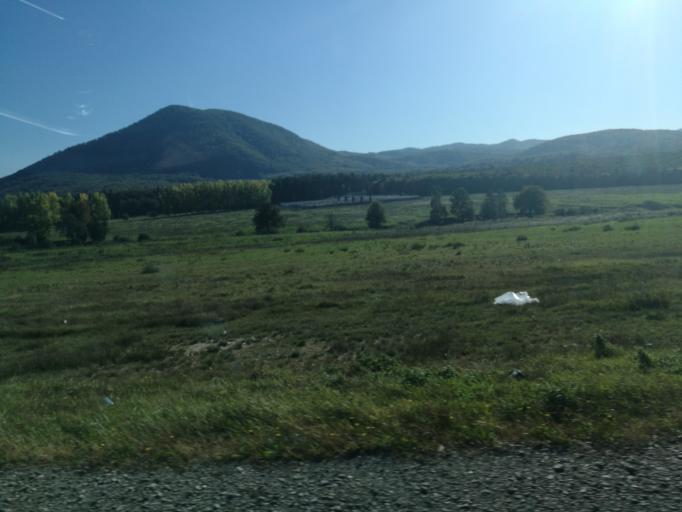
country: RO
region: Brasov
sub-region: Comuna Dumbravita
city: Dumbravita
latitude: 45.7486
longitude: 25.4100
